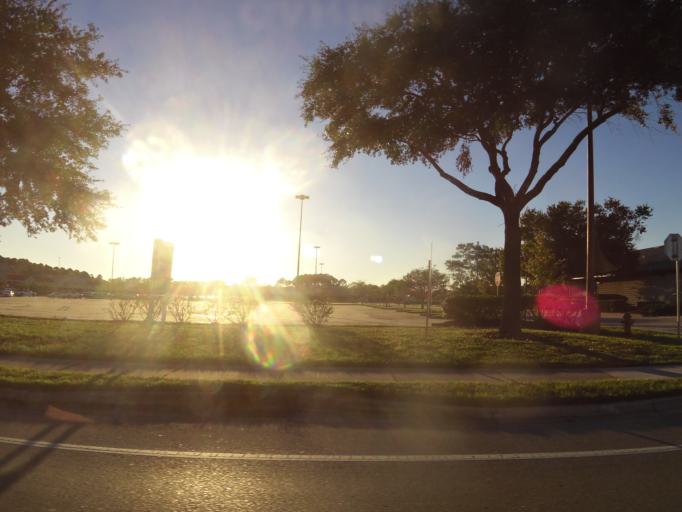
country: US
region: Florida
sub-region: Duval County
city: Jacksonville Beach
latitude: 30.2869
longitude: -81.4378
